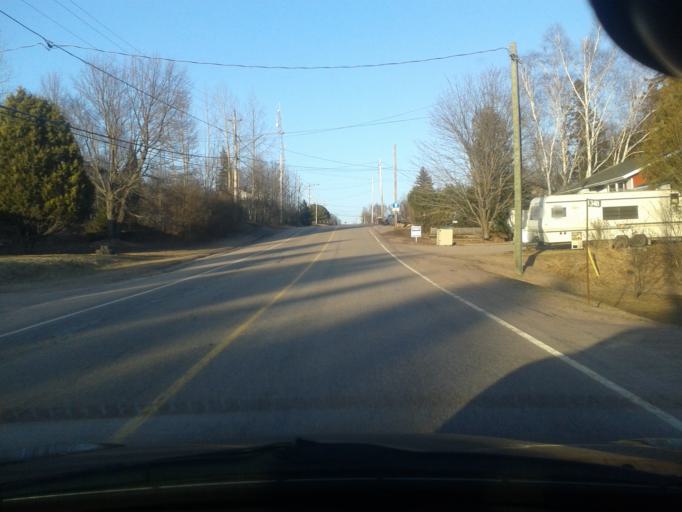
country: CA
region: Ontario
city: Powassan
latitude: 46.1857
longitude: -79.2829
